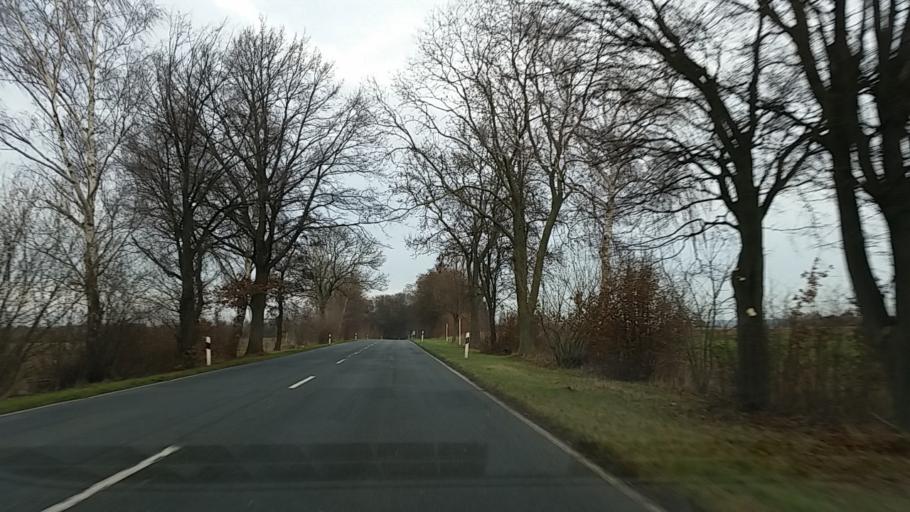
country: DE
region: Lower Saxony
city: Cramme
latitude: 52.0789
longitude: 10.4163
